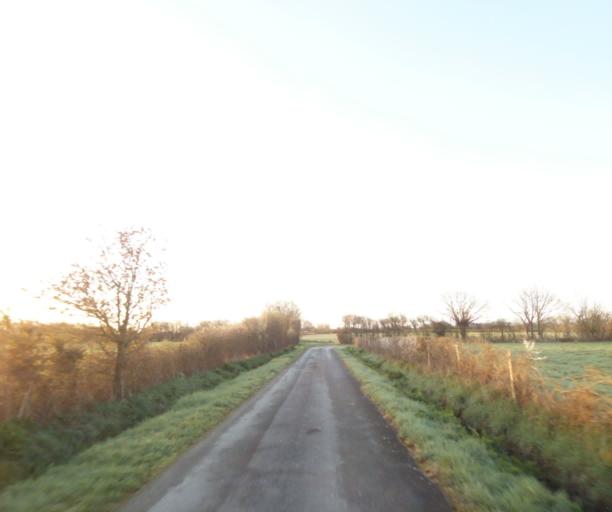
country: FR
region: Pays de la Loire
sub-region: Departement de la Loire-Atlantique
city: Bouvron
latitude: 47.4371
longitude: -1.8998
